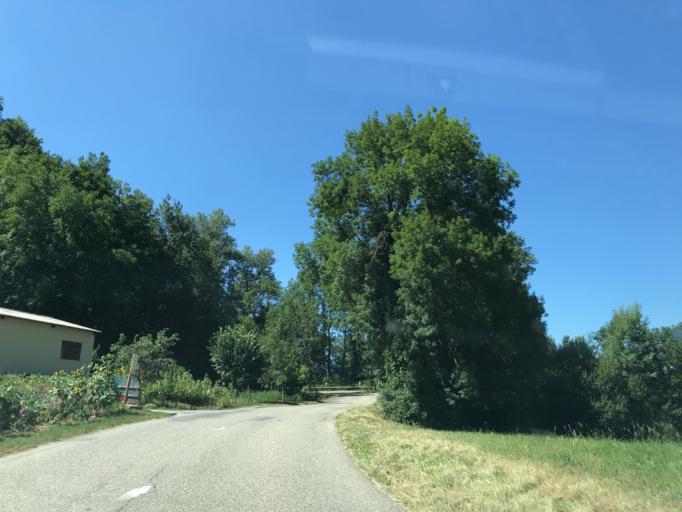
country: FR
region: Rhone-Alpes
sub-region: Departement de la Haute-Savoie
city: Villaz
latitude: 45.9274
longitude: 6.1763
